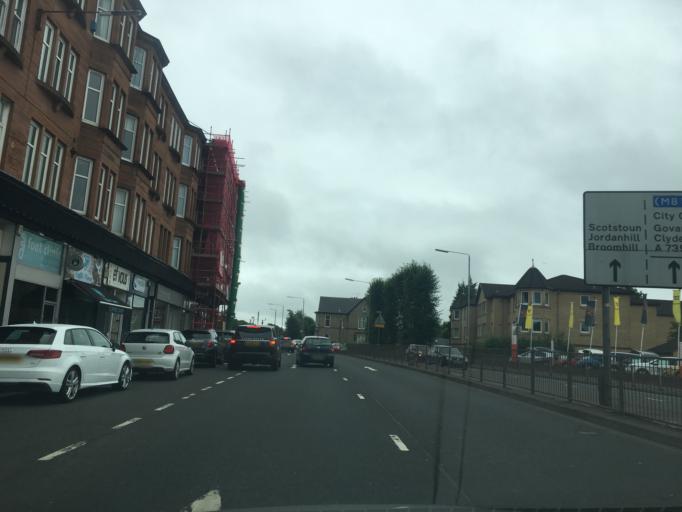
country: GB
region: Scotland
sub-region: East Dunbartonshire
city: Bearsden
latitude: 55.8818
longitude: -4.3261
